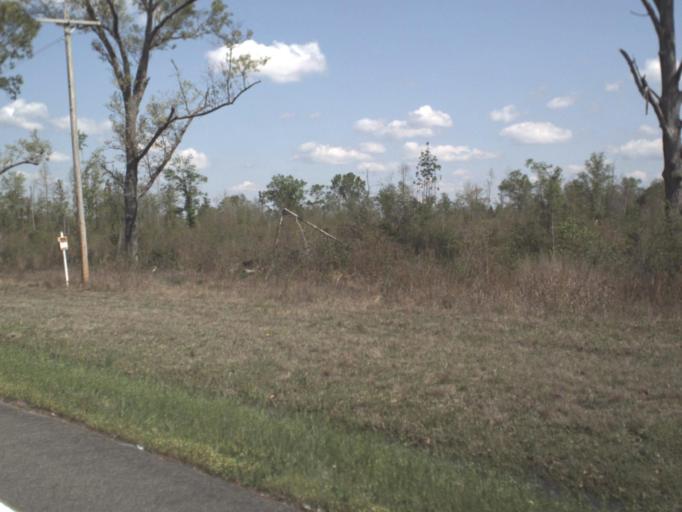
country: US
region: Alabama
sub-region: Escambia County
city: East Brewton
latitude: 30.9128
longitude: -87.0406
